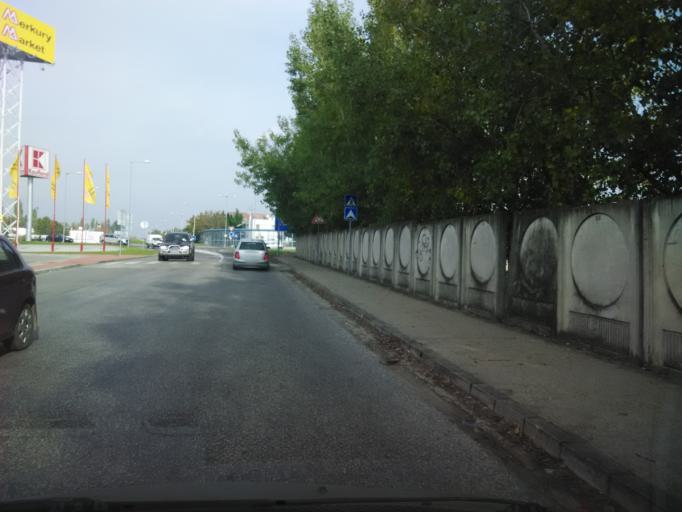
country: SK
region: Nitriansky
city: Komarno
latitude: 47.7646
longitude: 18.0951
